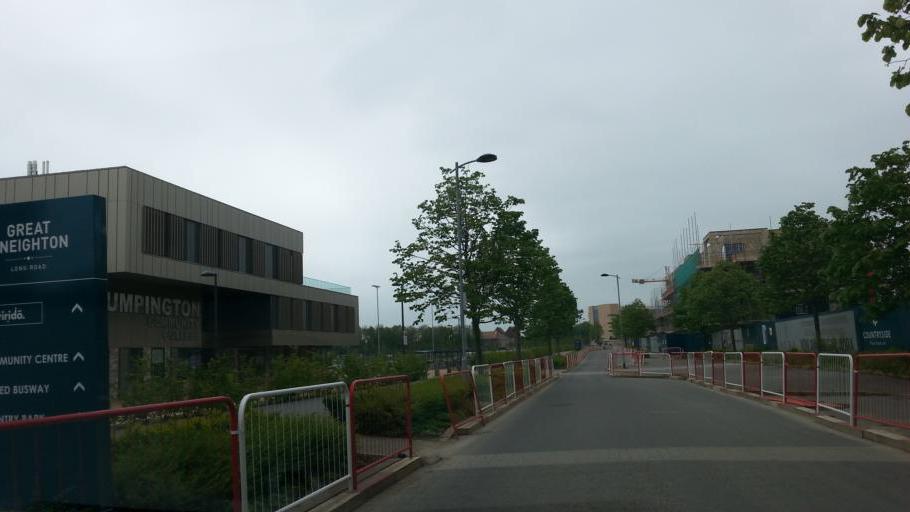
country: GB
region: England
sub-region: Cambridgeshire
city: Cambridge
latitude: 52.1766
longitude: 0.1227
